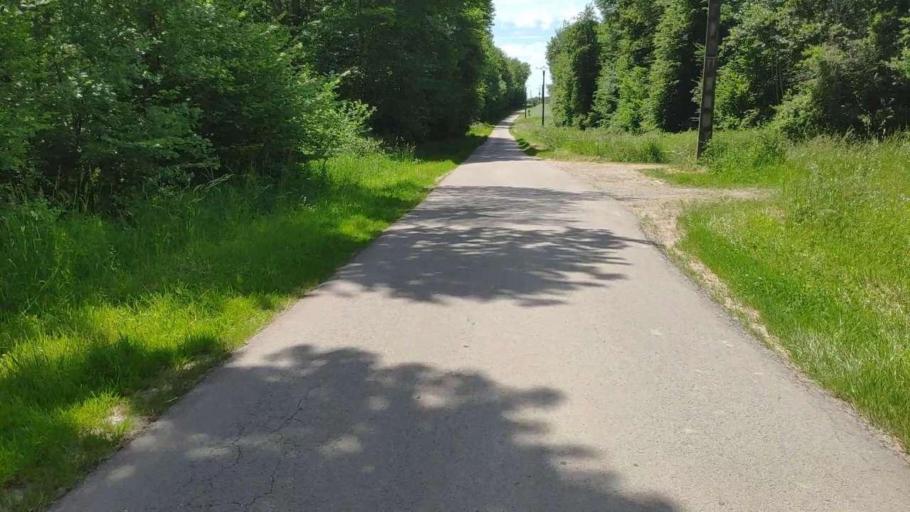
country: FR
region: Franche-Comte
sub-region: Departement du Jura
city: Bletterans
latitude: 46.7629
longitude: 5.4383
